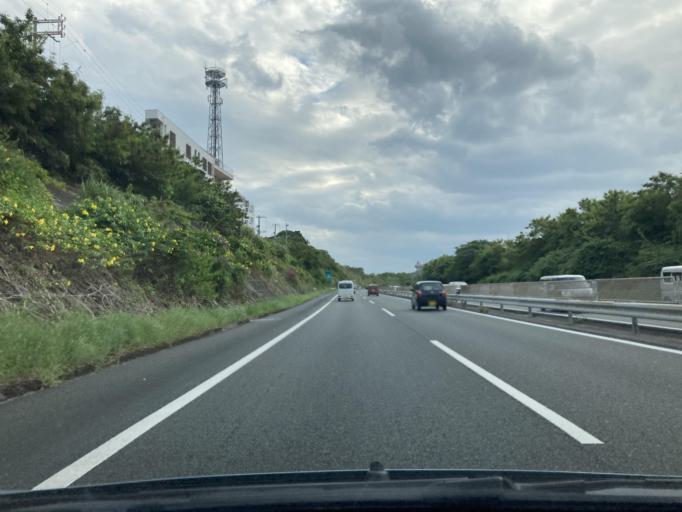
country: JP
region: Okinawa
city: Ginowan
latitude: 26.2536
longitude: 127.7620
